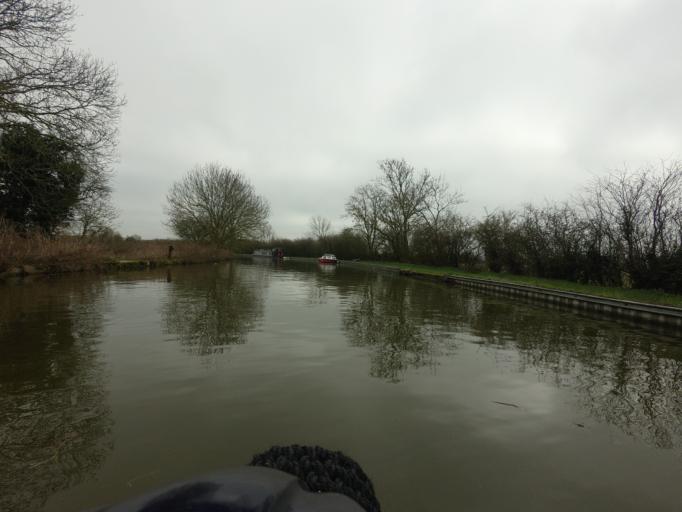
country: GB
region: England
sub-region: Buckinghamshire
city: Cheddington
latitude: 51.8746
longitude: -0.6556
